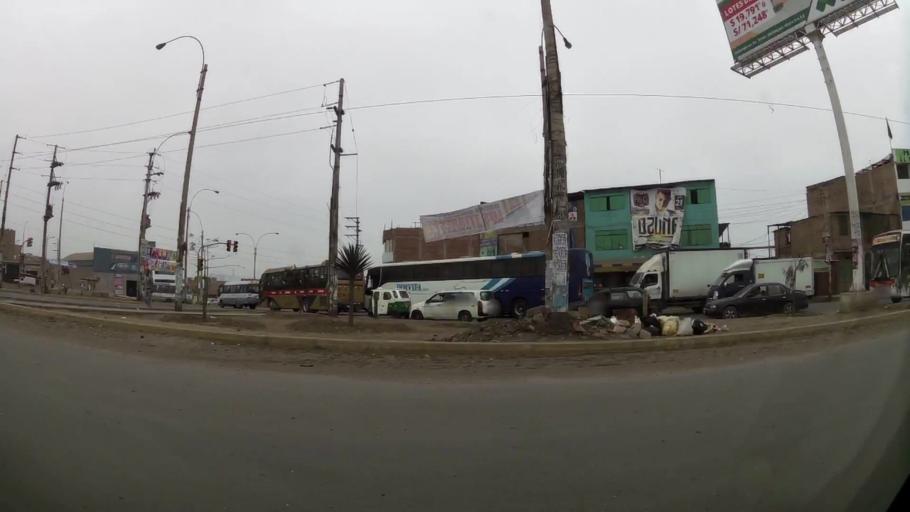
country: PE
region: Lima
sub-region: Lima
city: Punta Hermosa
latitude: -12.2399
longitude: -76.9127
